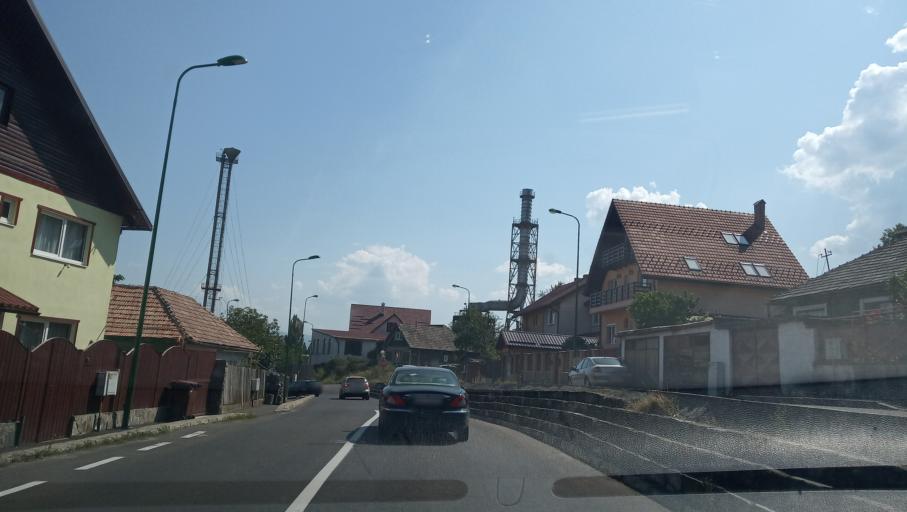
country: RO
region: Brasov
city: Brasov
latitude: 45.6365
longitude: 25.6168
